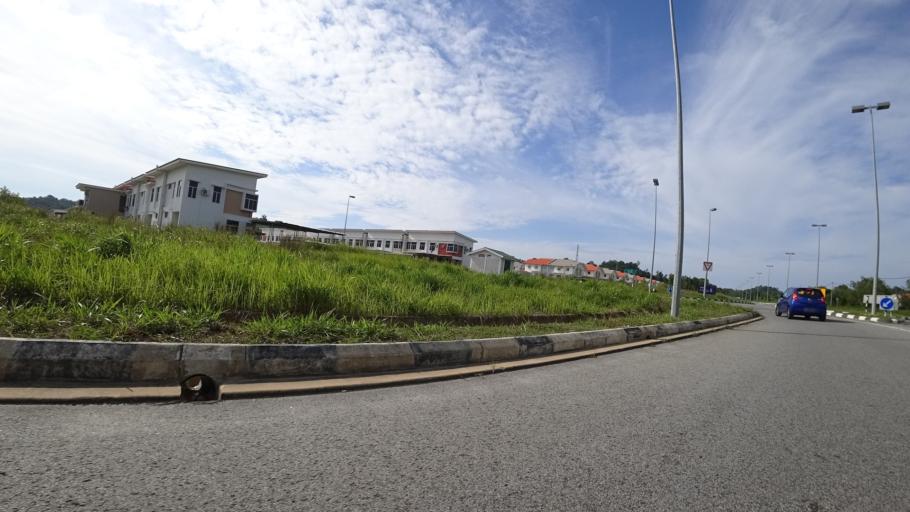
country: BN
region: Brunei and Muara
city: Bandar Seri Begawan
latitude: 4.8912
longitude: 114.8035
